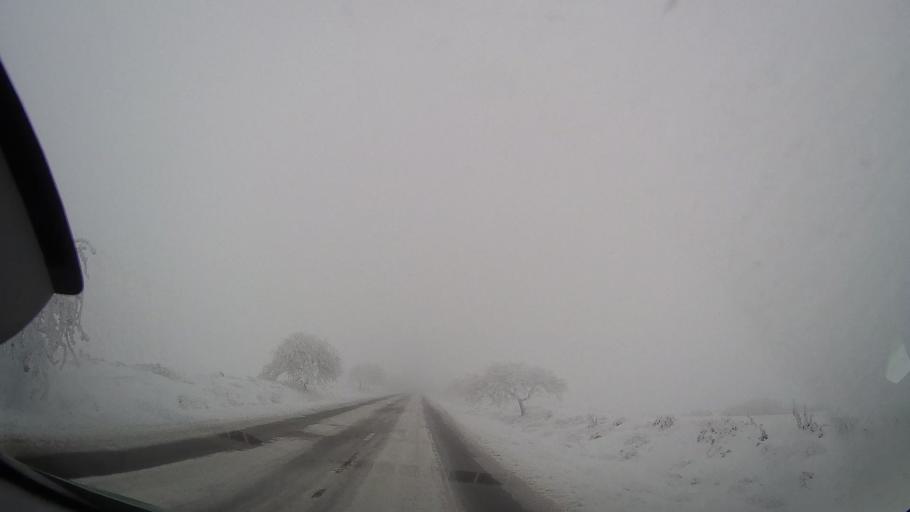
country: RO
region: Neamt
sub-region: Comuna Valea Ursului
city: Valea Ursului
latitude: 46.8208
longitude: 27.0639
